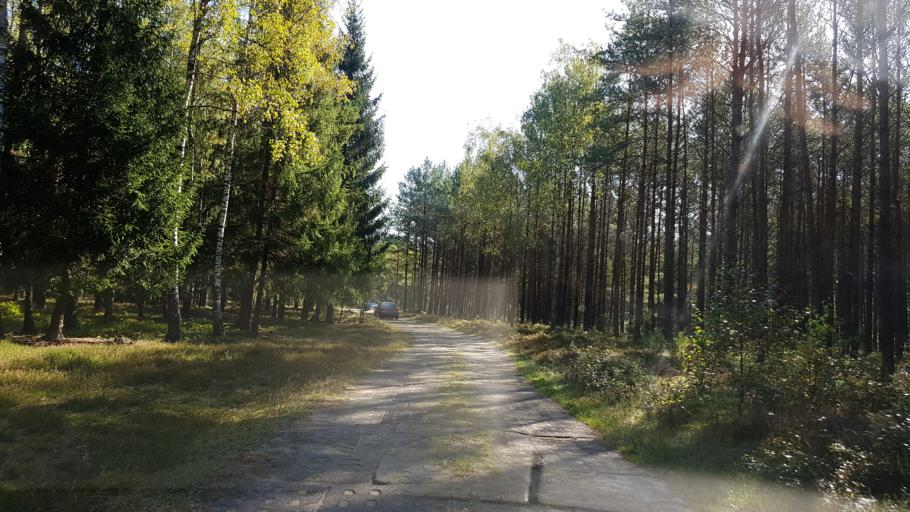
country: PL
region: West Pomeranian Voivodeship
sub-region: Powiat koszalinski
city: Bobolice
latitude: 54.0532
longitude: 16.5972
